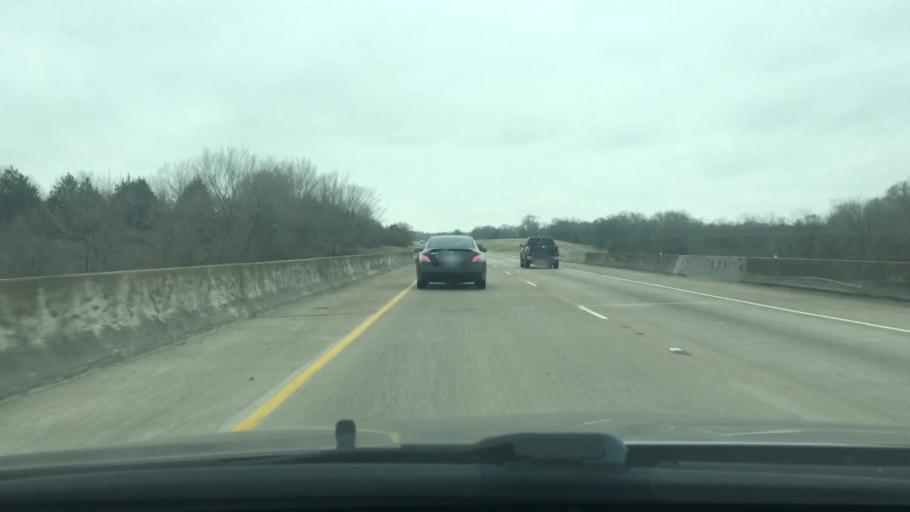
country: US
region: Texas
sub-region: Freestone County
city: Fairfield
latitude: 31.7957
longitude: -96.2536
